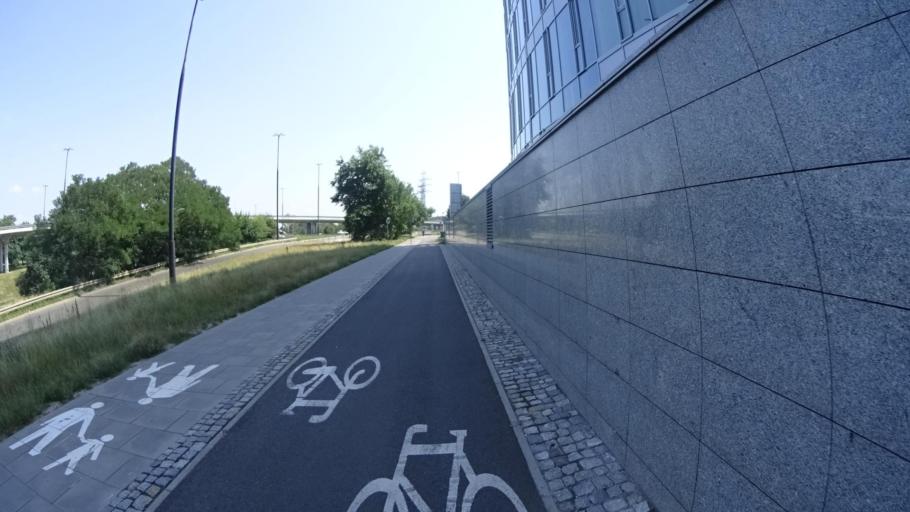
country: PL
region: Masovian Voivodeship
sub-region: Warszawa
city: Mokotow
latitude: 52.1667
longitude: 21.0153
